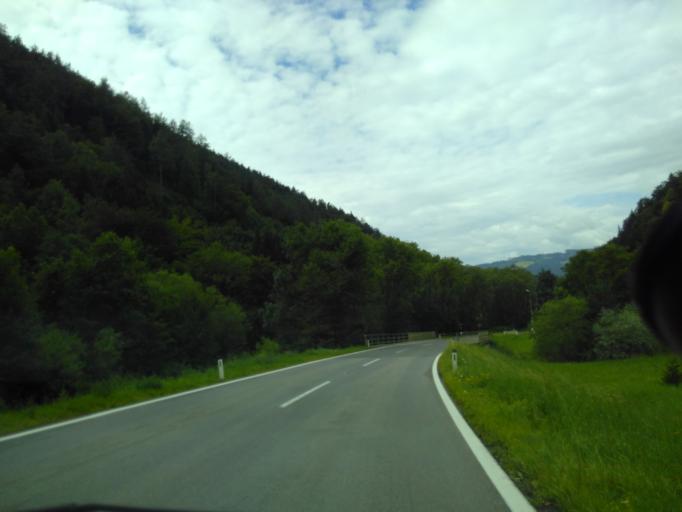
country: AT
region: Styria
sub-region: Politischer Bezirk Graz-Umgebung
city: Schrems bei Frohnleiten
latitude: 47.2723
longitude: 15.3434
